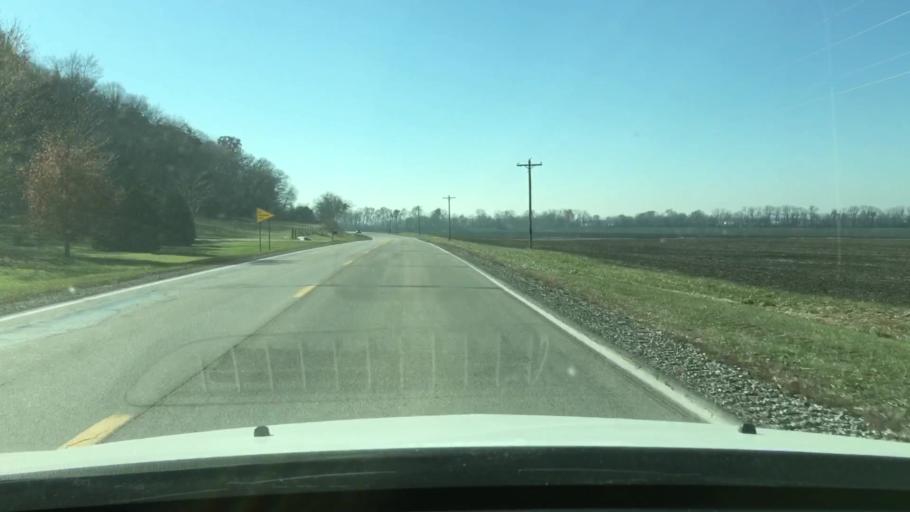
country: US
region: Illinois
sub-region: Morgan County
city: Meredosia
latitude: 39.7278
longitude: -90.5661
